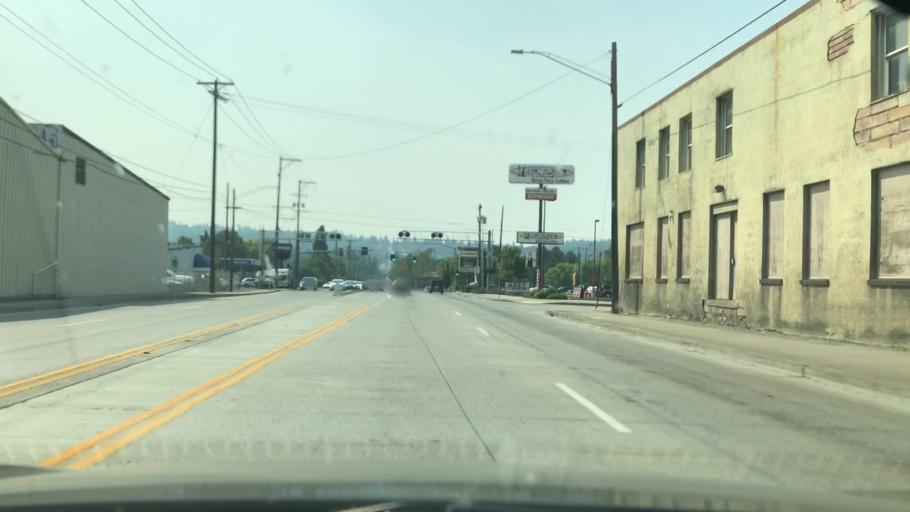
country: US
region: Washington
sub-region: Spokane County
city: Spokane
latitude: 47.6586
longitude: -117.3577
